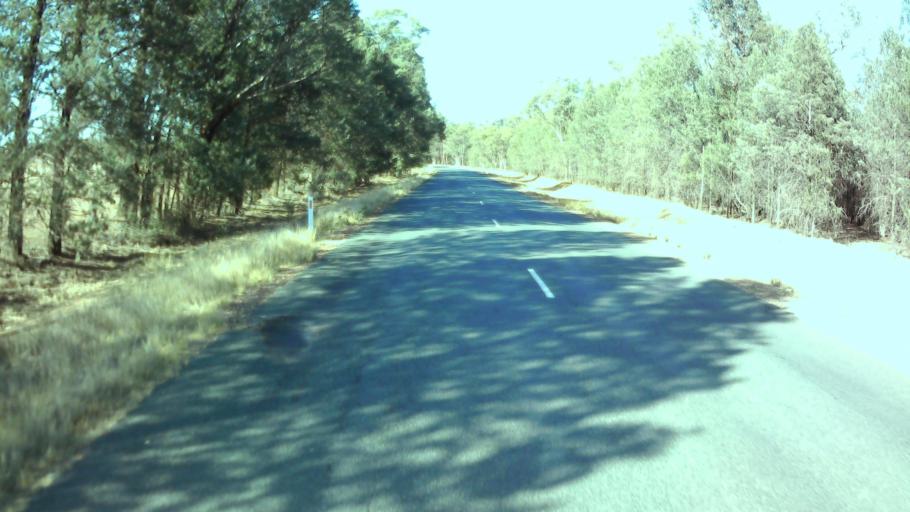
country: AU
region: New South Wales
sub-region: Weddin
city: Grenfell
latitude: -34.0206
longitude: 148.1025
